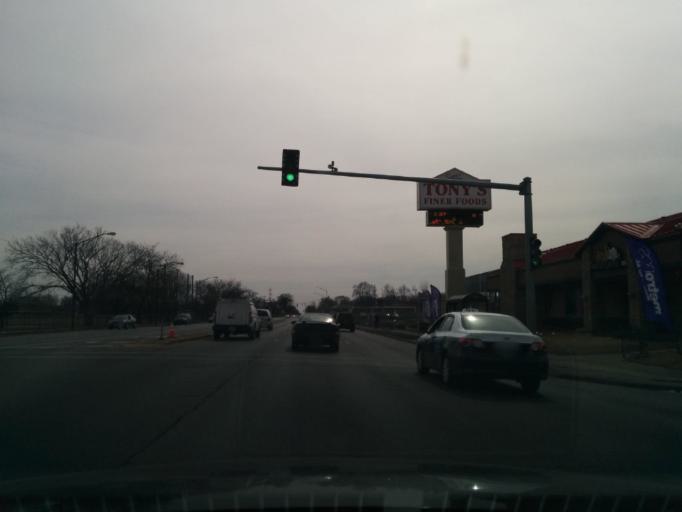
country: US
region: Illinois
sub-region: Cook County
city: Berwyn
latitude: 41.8461
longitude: -87.8036
